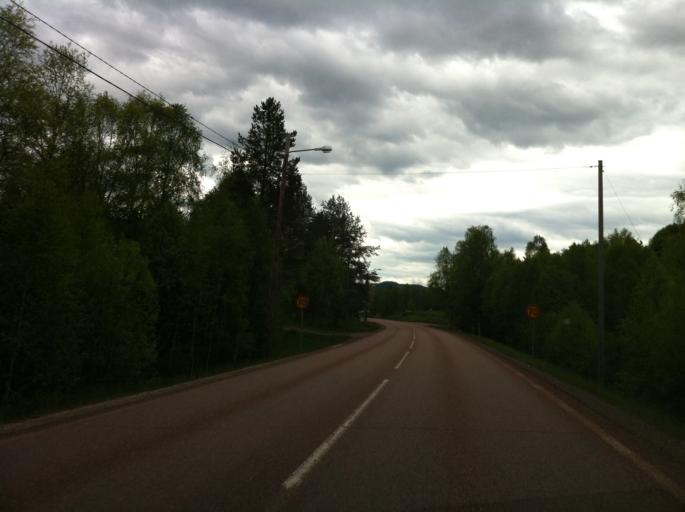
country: SE
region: Dalarna
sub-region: Malung-Saelens kommun
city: Malung
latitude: 61.0869
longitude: 13.3221
